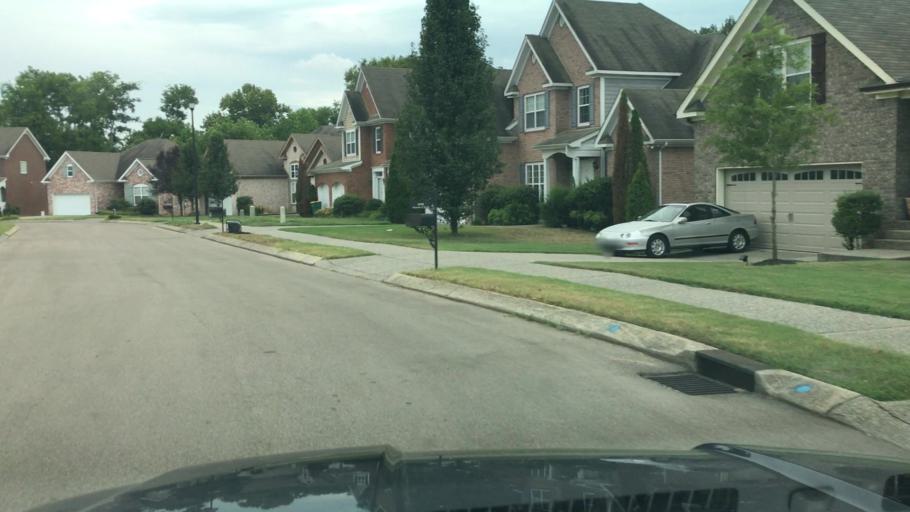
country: US
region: Tennessee
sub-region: Maury County
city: Spring Hill
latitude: 35.7574
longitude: -86.8752
